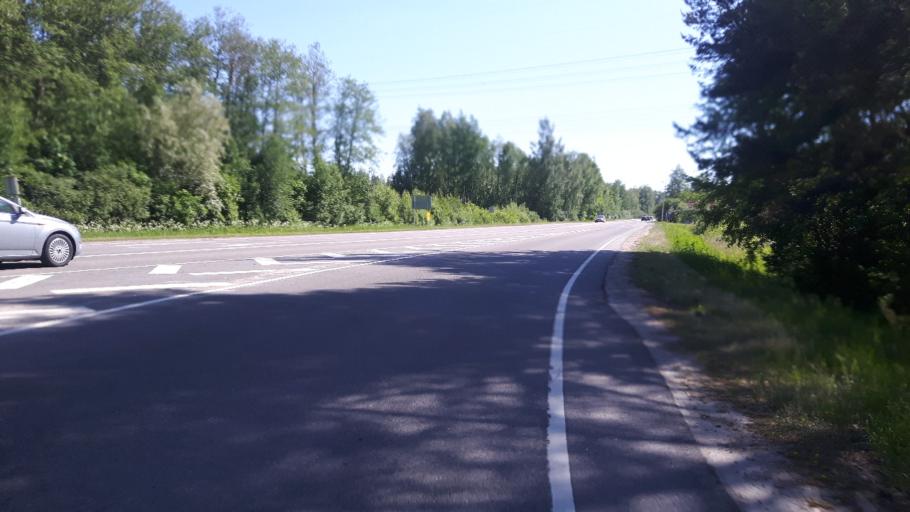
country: EE
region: Paernumaa
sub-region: Paikuse vald
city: Paikuse
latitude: 58.3903
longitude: 24.6413
